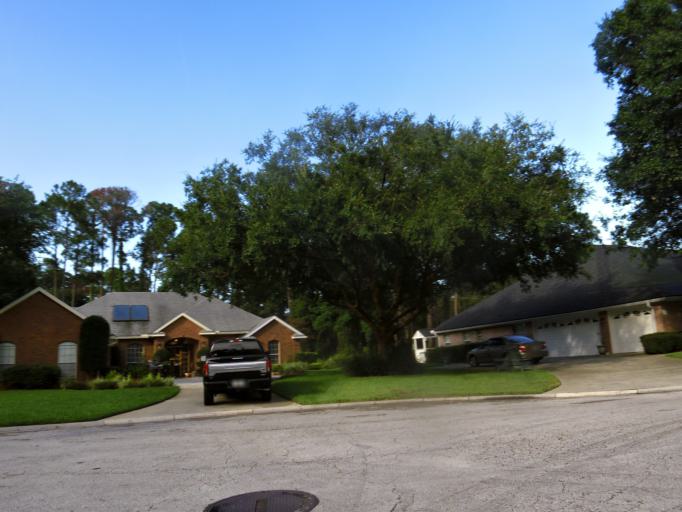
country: US
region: Florida
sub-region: Saint Johns County
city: Fruit Cove
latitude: 30.2110
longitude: -81.5354
